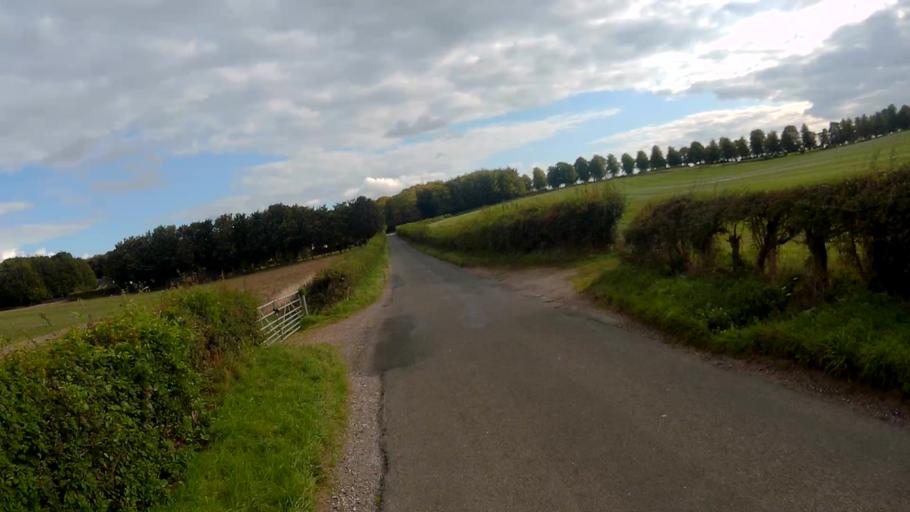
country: GB
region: England
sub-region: Hampshire
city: Kings Worthy
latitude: 51.1363
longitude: -1.2113
